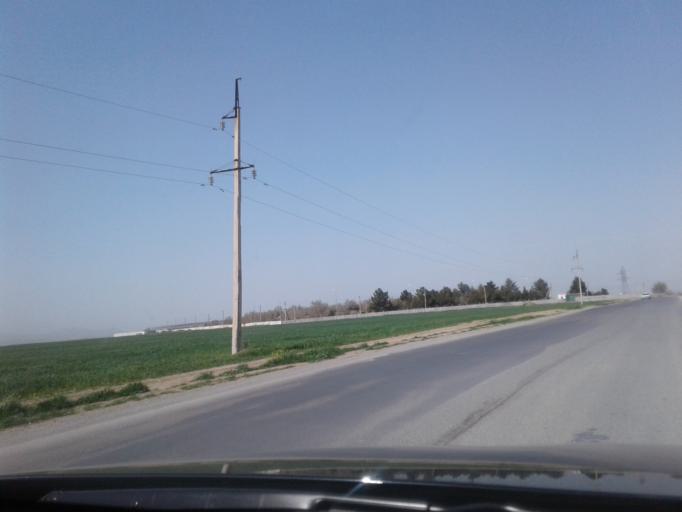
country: TM
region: Ahal
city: Abadan
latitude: 38.1851
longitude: 57.9743
